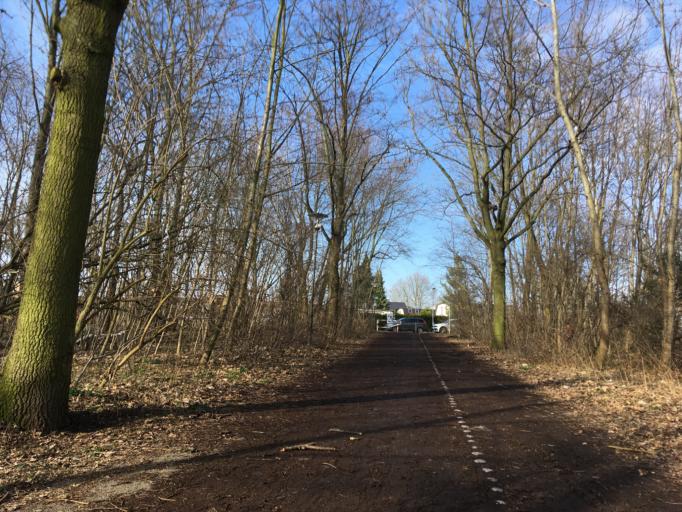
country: DE
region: Berlin
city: Rosenthal
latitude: 52.6140
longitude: 13.3699
